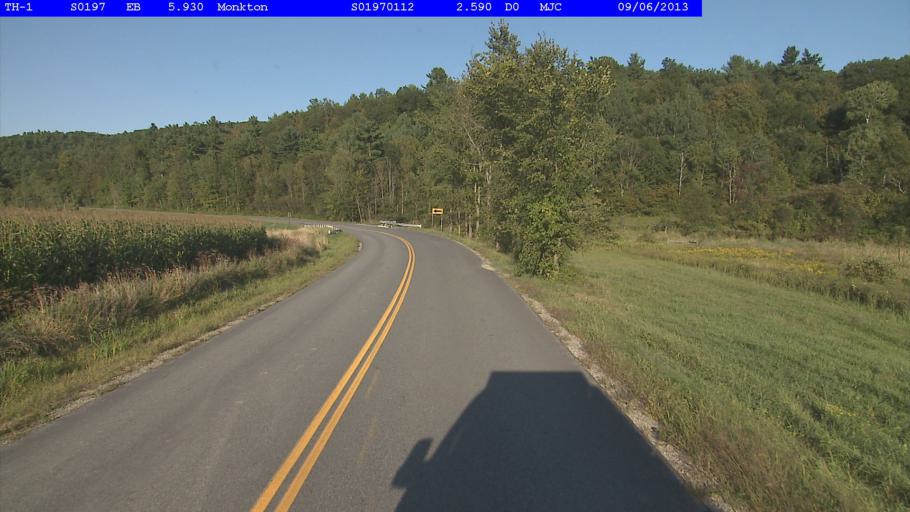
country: US
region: Vermont
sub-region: Addison County
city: Vergennes
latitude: 44.2160
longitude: -73.1570
